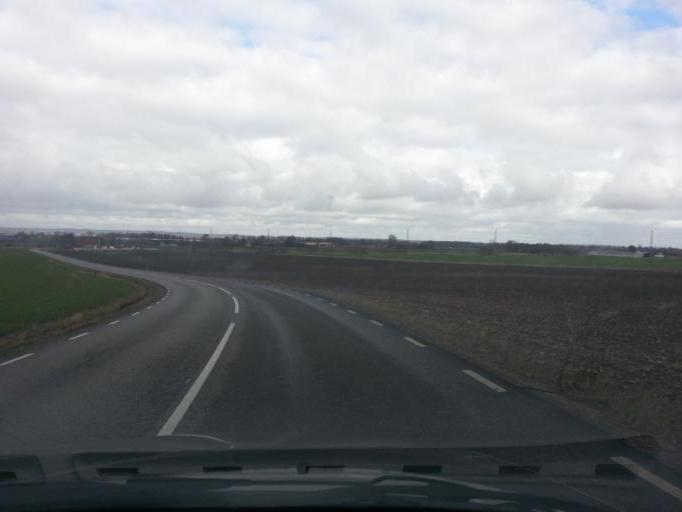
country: SE
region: Skane
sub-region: Astorps Kommun
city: Astorp
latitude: 56.1293
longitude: 13.0023
